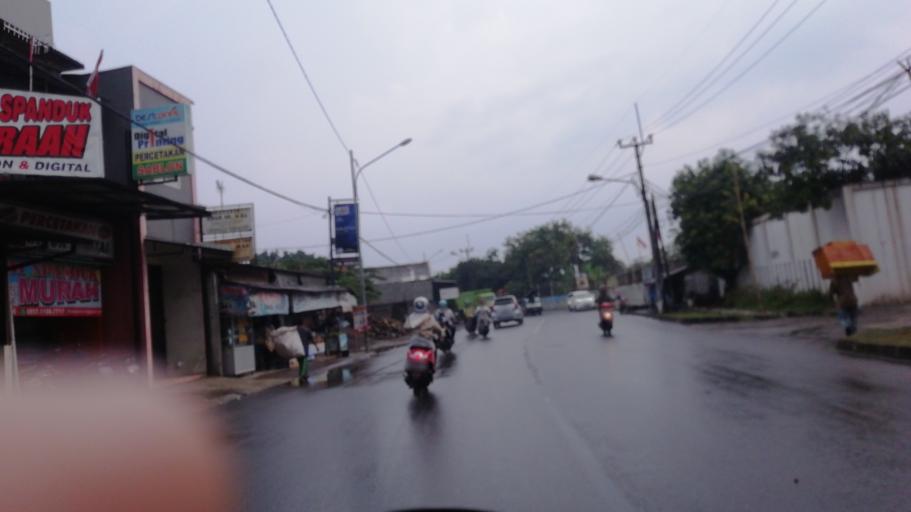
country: ID
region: West Java
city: Cibinong
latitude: -6.5267
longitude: 106.8096
